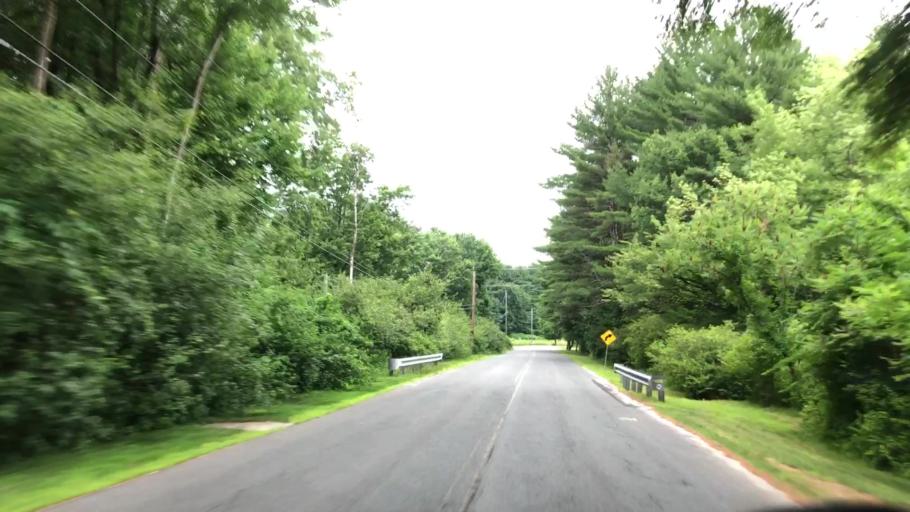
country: US
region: Massachusetts
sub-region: Hampshire County
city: Southampton
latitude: 42.2194
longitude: -72.6832
